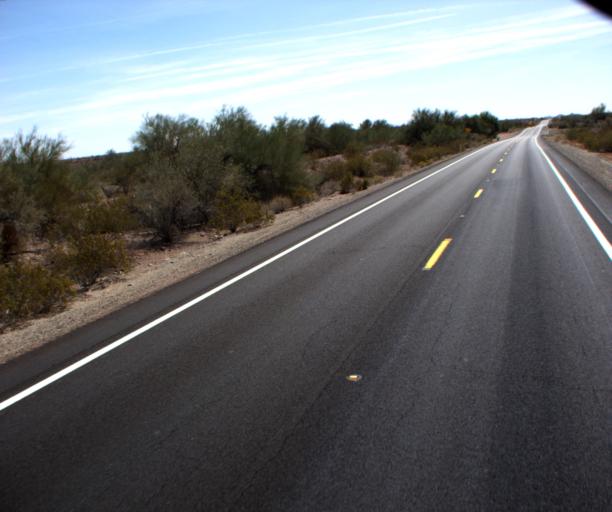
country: US
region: Arizona
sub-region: La Paz County
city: Quartzsite
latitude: 33.1683
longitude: -114.2775
